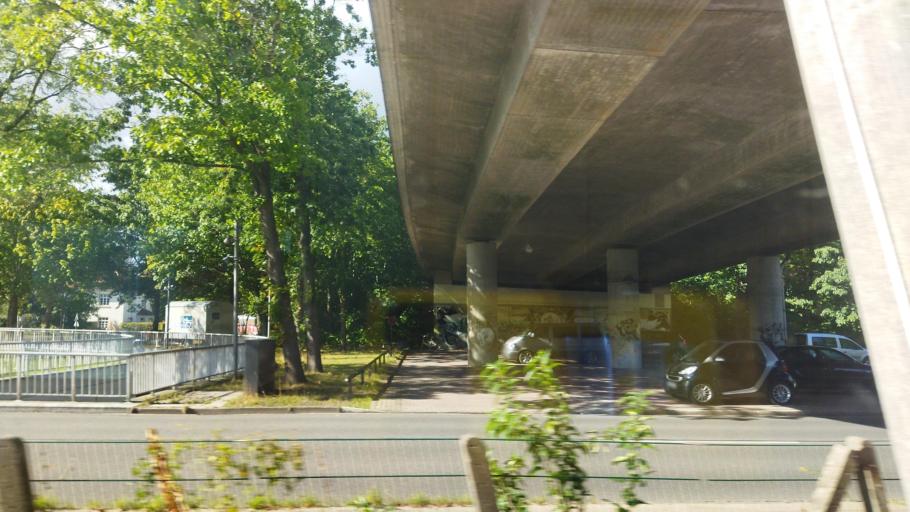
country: DE
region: Lower Saxony
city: Lingen
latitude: 52.5255
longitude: 7.3255
